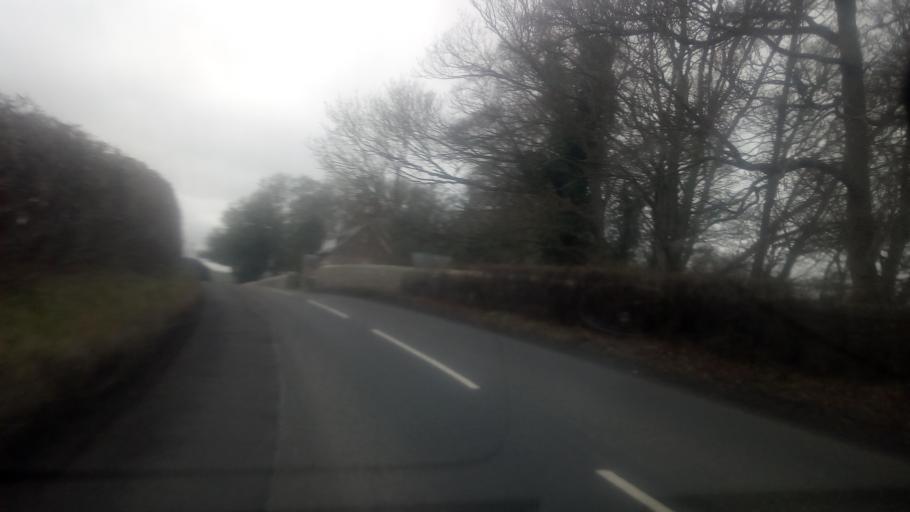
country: GB
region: Scotland
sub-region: The Scottish Borders
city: Kelso
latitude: 55.5938
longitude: -2.4632
